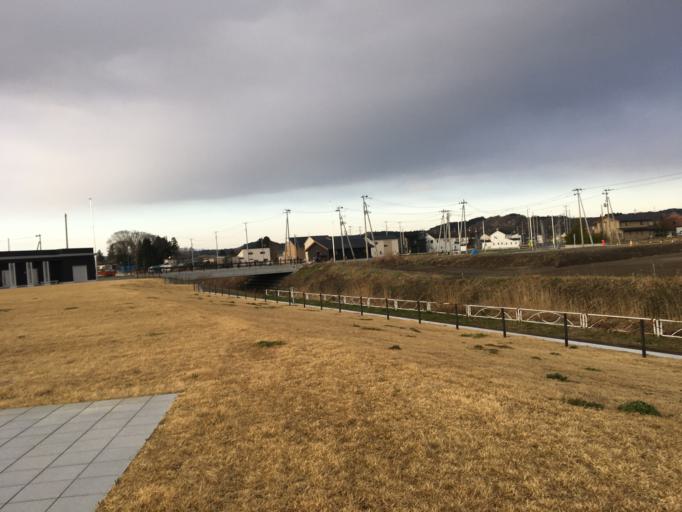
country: JP
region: Aomori
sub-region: Hachinohe Shi
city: Uchimaru
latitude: 40.5103
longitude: 141.4266
